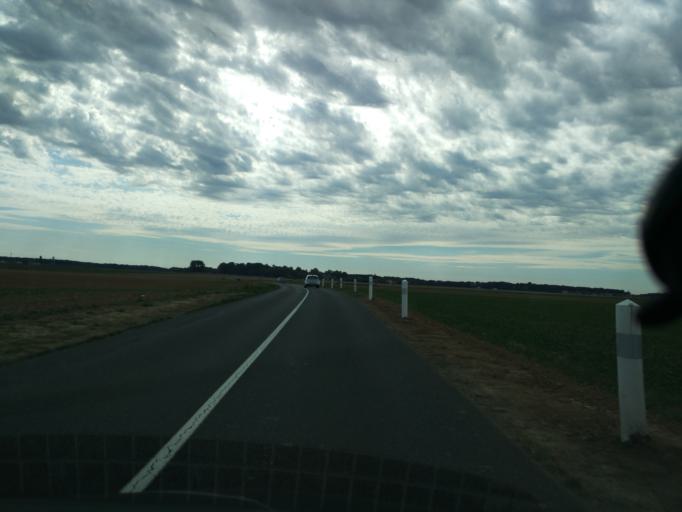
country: FR
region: Ile-de-France
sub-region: Departement de l'Essonne
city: Gometz-la-Ville
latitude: 48.6590
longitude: 2.1249
